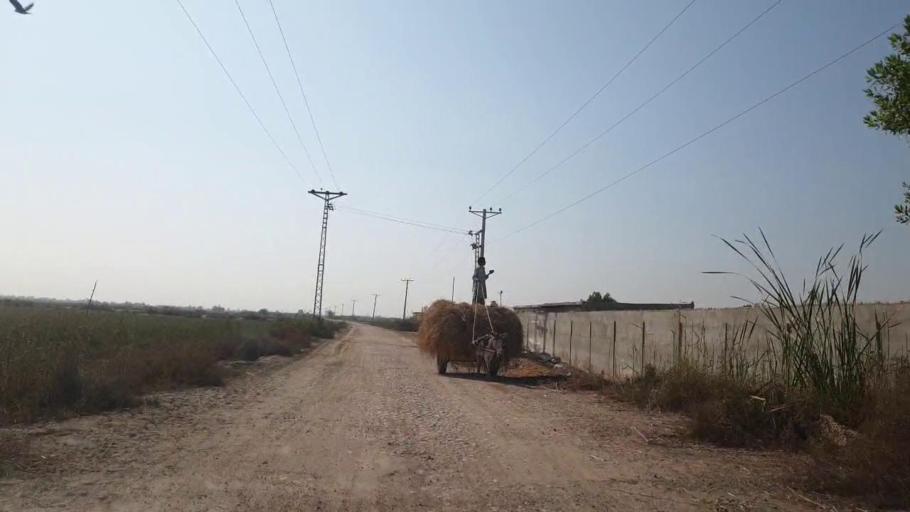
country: PK
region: Sindh
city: Thatta
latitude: 24.7383
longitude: 67.7944
